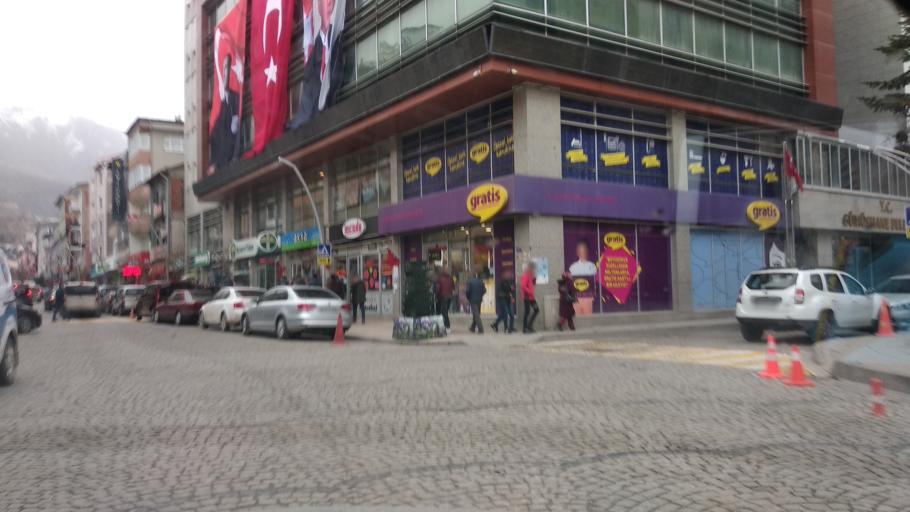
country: TR
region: Gumushane
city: Gumushkhane
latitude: 40.4589
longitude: 39.4784
